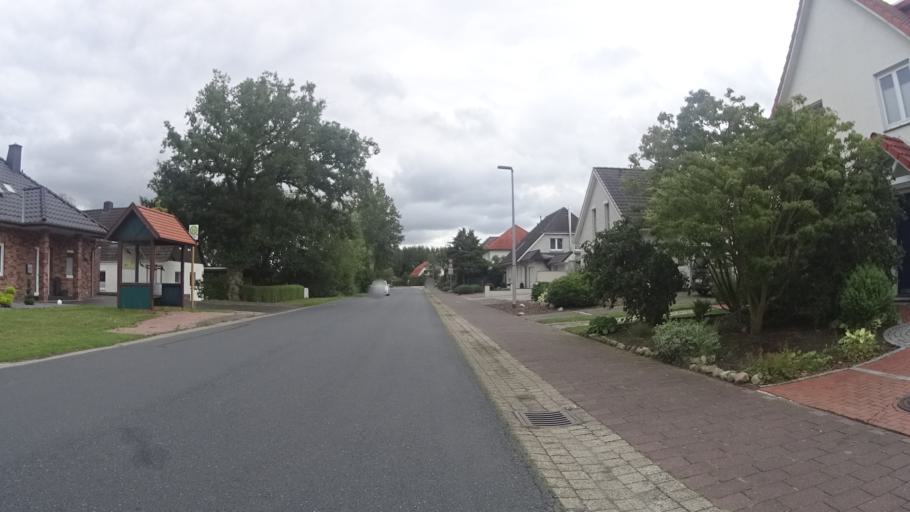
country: DE
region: Lower Saxony
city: Schiffdorf
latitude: 53.5344
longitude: 8.6623
